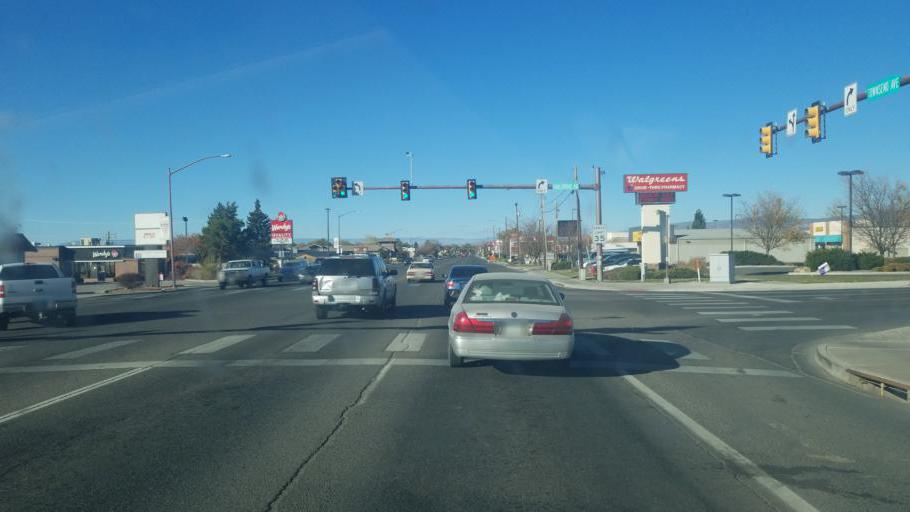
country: US
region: Colorado
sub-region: Montrose County
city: Montrose
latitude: 38.4597
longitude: -107.8662
